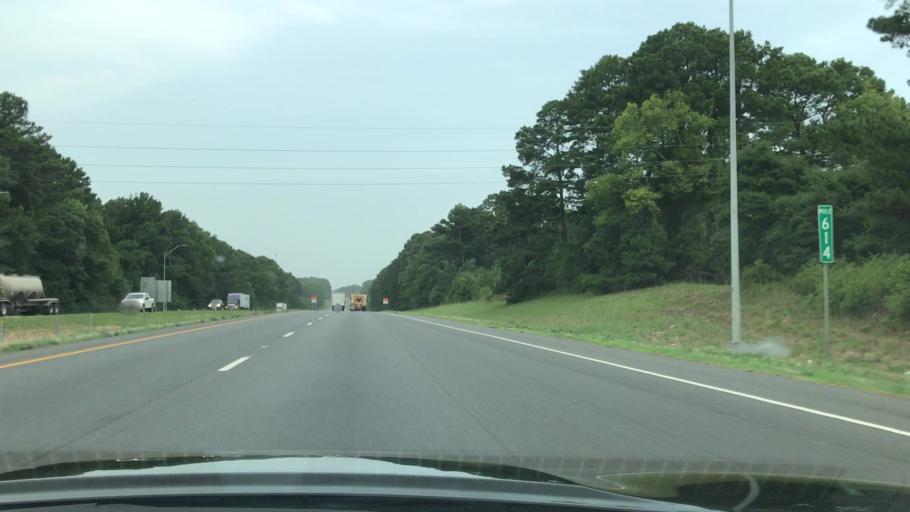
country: US
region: Texas
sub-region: Harrison County
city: Marshall
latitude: 32.4889
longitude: -94.4141
